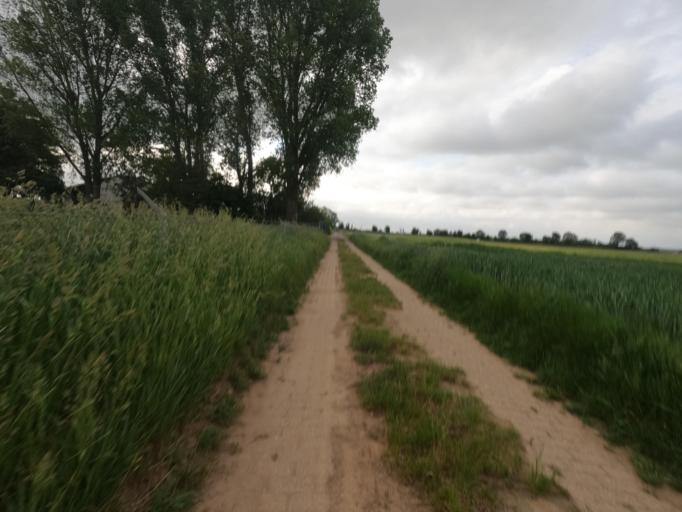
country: DE
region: North Rhine-Westphalia
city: Huckelhoven
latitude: 51.0478
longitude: 6.2008
